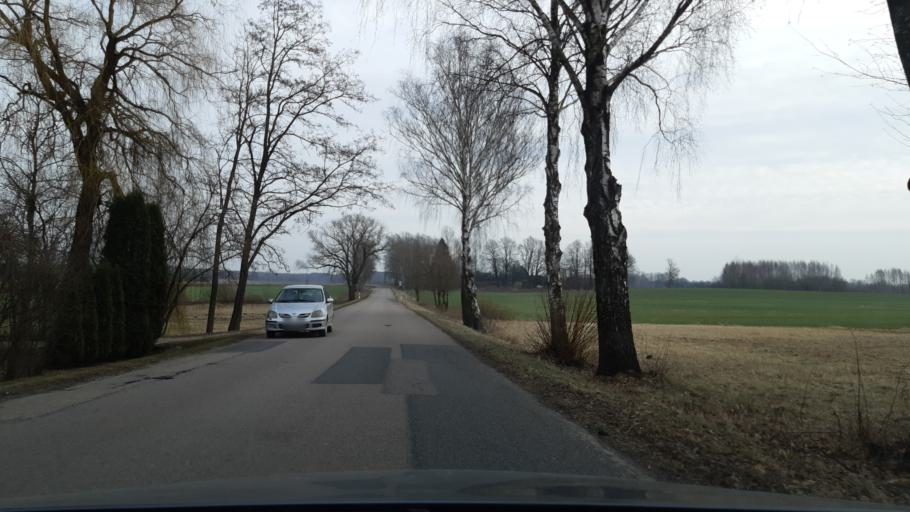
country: LT
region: Marijampoles apskritis
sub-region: Marijampole Municipality
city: Marijampole
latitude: 54.7177
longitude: 23.3264
